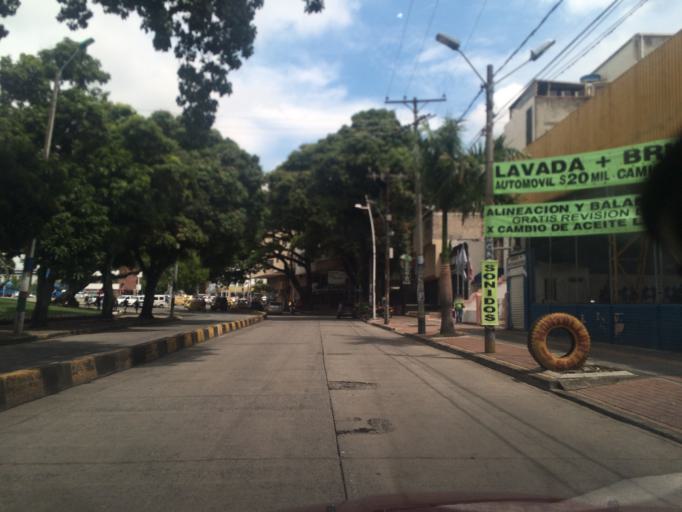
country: CO
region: Valle del Cauca
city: Cali
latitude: 3.4318
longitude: -76.5416
